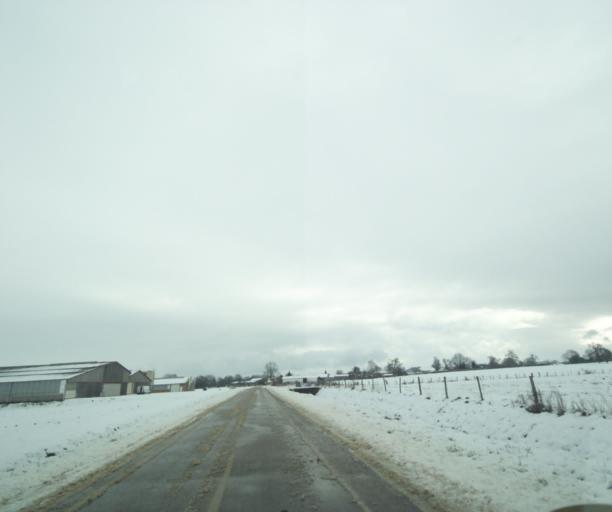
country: FR
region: Champagne-Ardenne
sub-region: Departement de la Haute-Marne
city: Montier-en-Der
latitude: 48.4409
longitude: 4.7082
